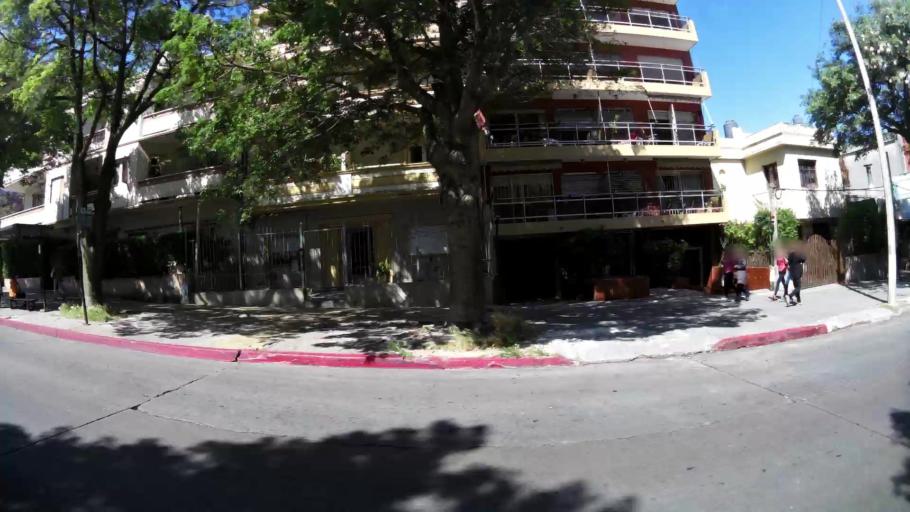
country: UY
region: Montevideo
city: Montevideo
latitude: -34.9054
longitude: -56.1550
